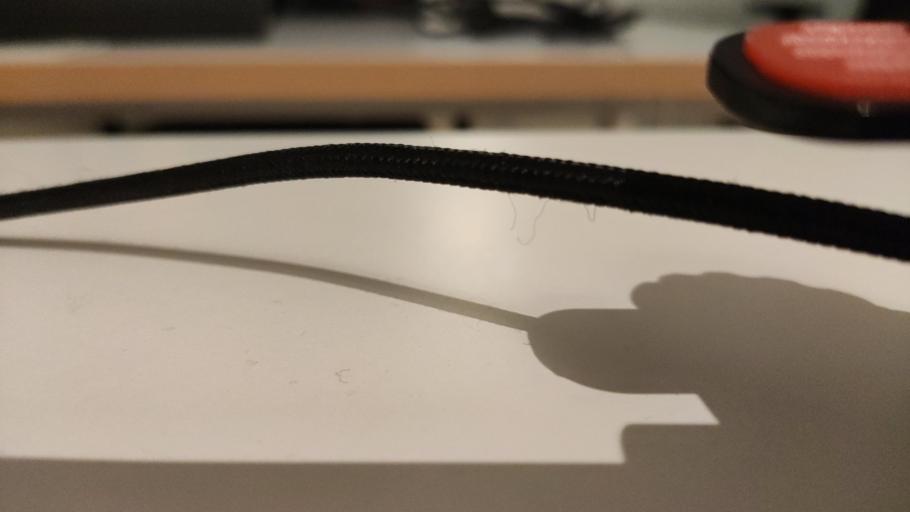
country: RU
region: Moskovskaya
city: Novosin'kovo
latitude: 56.3962
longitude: 37.2723
